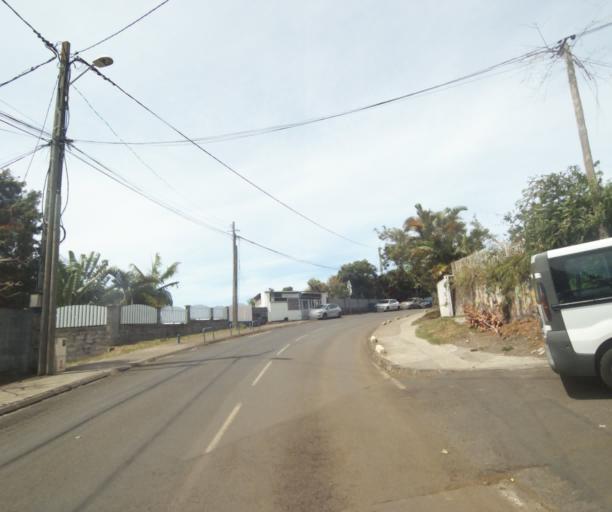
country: RE
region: Reunion
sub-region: Reunion
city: Saint-Paul
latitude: -21.0469
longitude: 55.2848
